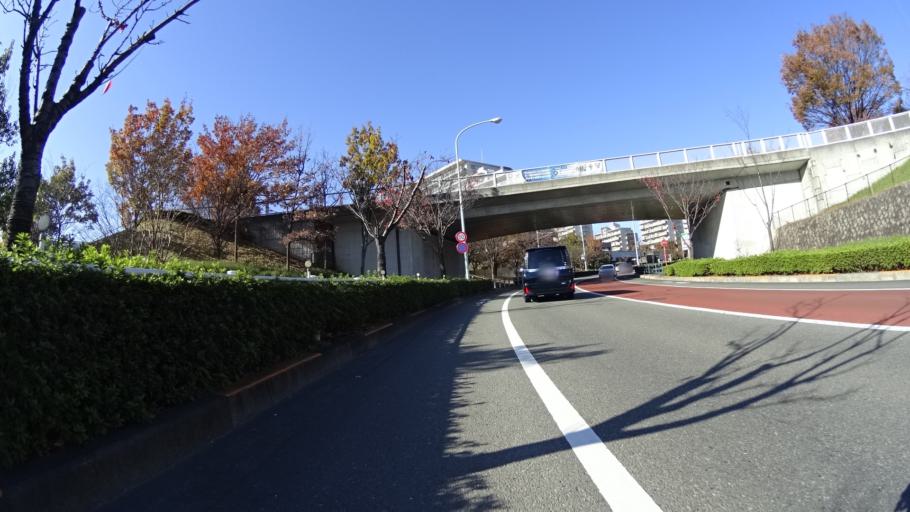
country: JP
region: Tokyo
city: Kokubunji
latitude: 35.6270
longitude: 139.4731
